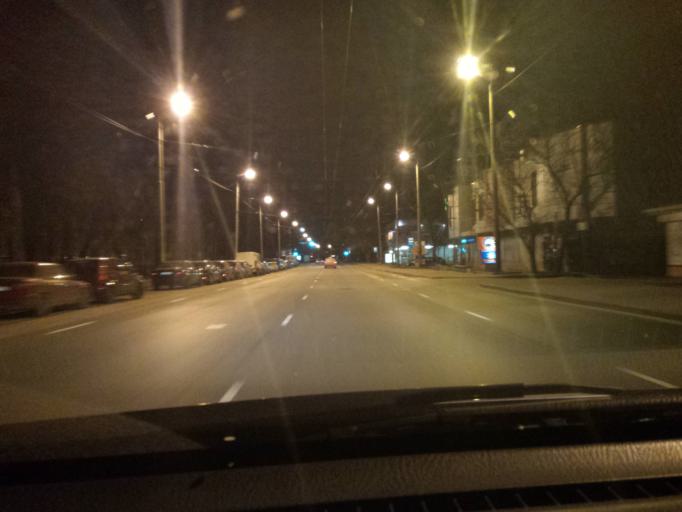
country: LV
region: Riga
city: Riga
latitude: 56.9611
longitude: 24.1758
